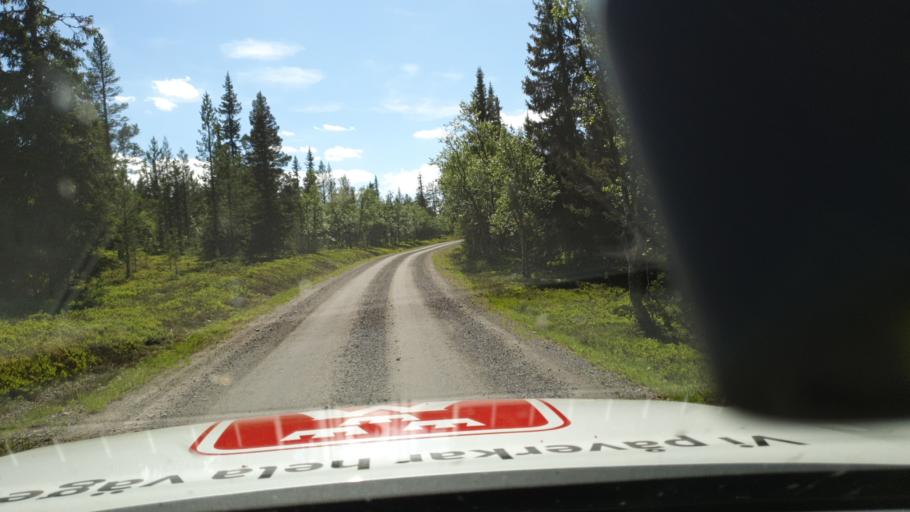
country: NO
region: Hedmark
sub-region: Engerdal
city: Engerdal
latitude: 62.1424
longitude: 12.9469
